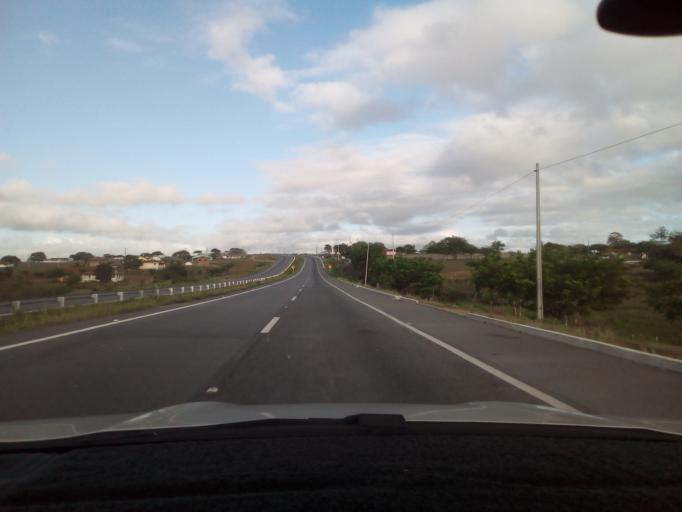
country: BR
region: Paraiba
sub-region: Serra Redonda
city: Alagoa Grande
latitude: -7.2026
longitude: -35.5508
